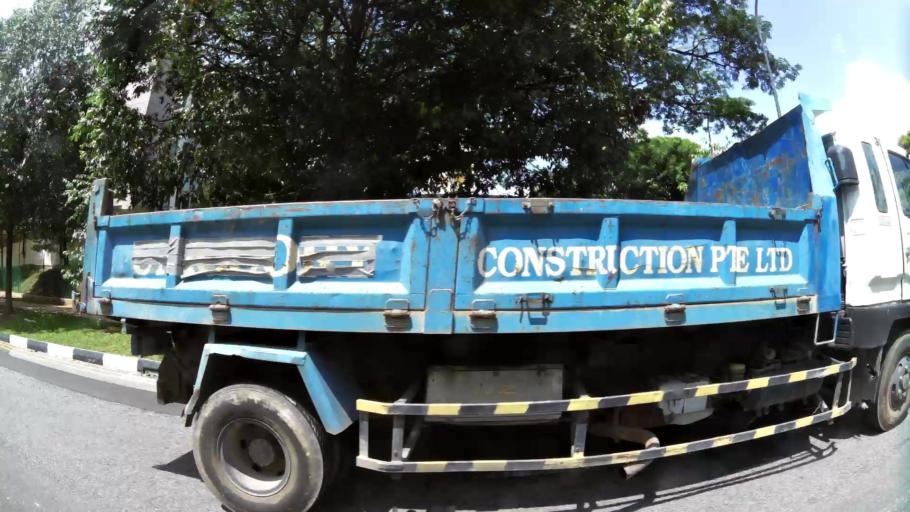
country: SG
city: Singapore
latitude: 1.3673
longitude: 103.8359
